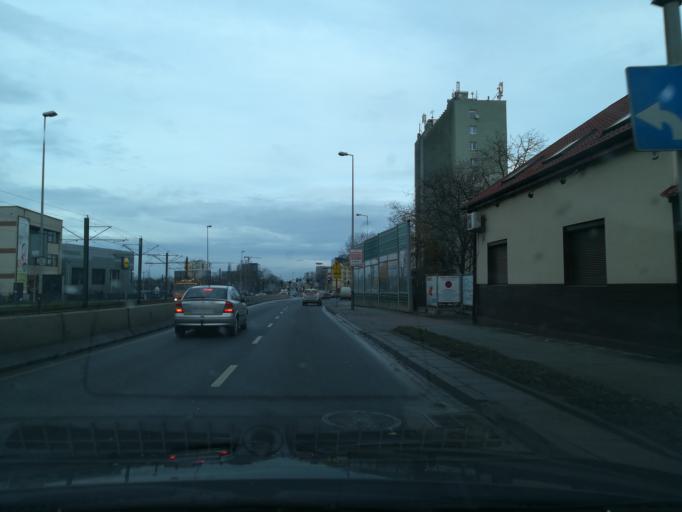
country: PL
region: Lesser Poland Voivodeship
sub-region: Krakow
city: Krakow
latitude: 50.0275
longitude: 19.9358
